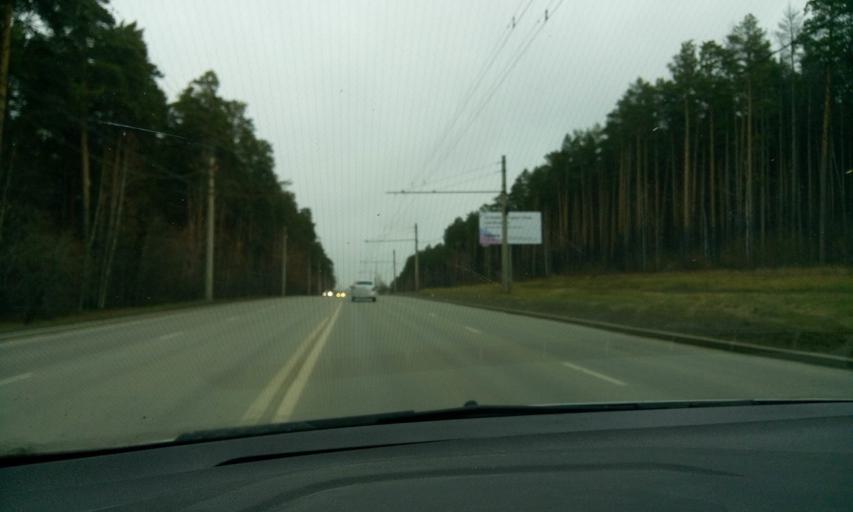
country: RU
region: Sverdlovsk
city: Sovkhoznyy
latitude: 56.7854
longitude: 60.5654
